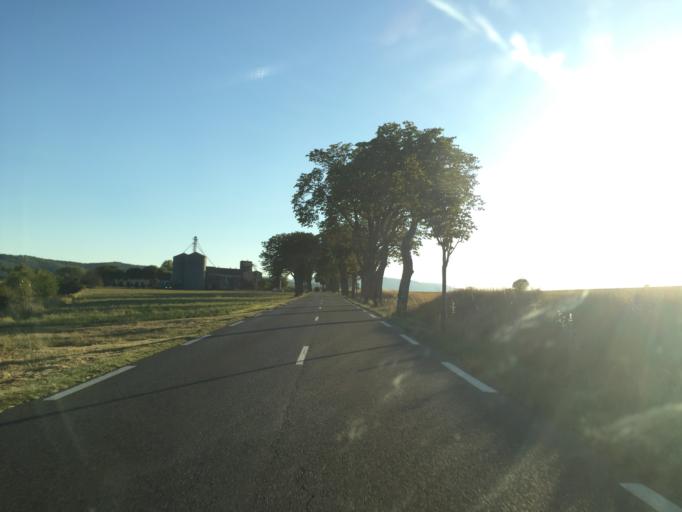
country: FR
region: Provence-Alpes-Cote d'Azur
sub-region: Departement des Alpes-de-Haute-Provence
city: Reillanne
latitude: 43.8661
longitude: 5.6843
